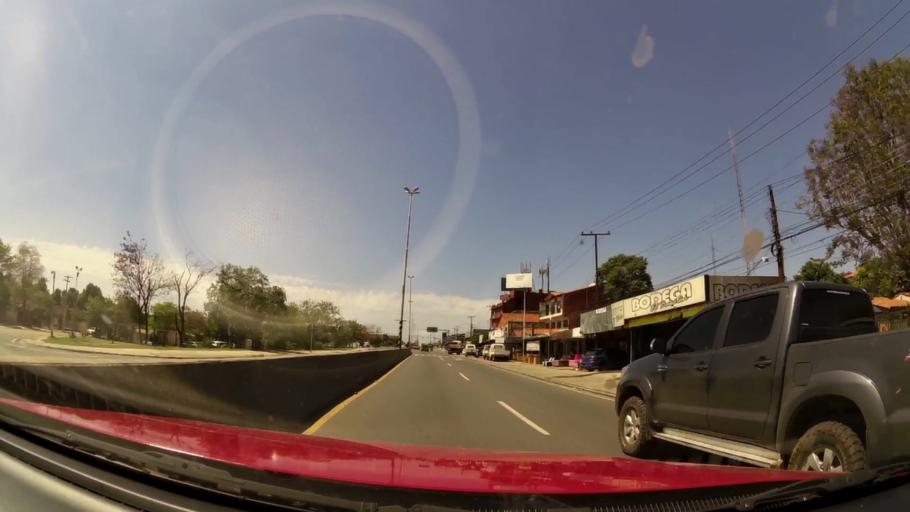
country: PY
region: Central
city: Colonia Mariano Roque Alonso
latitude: -25.2484
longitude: -57.5514
